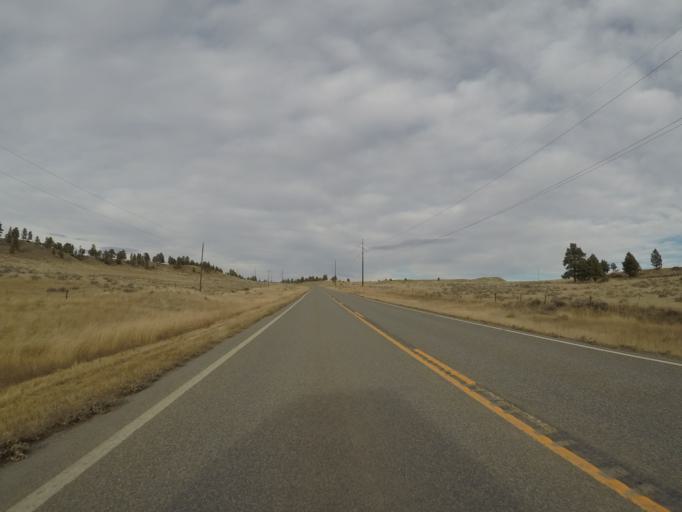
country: US
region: Montana
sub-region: Yellowstone County
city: Laurel
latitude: 45.8349
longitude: -108.7226
